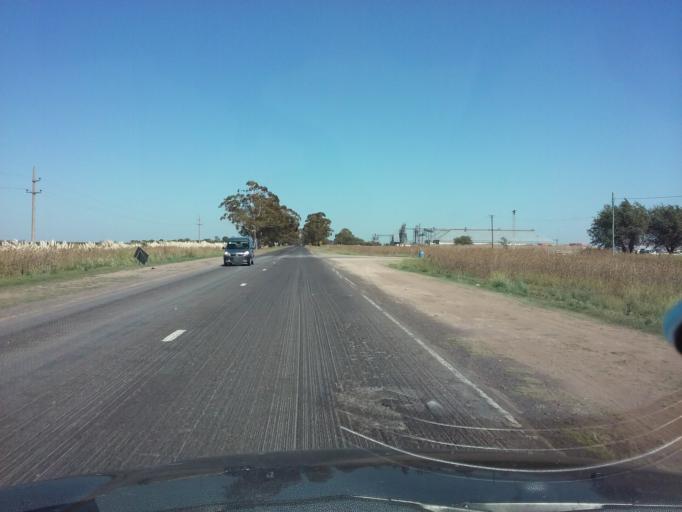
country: AR
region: La Pampa
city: General Pico
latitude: -35.6988
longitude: -63.7945
